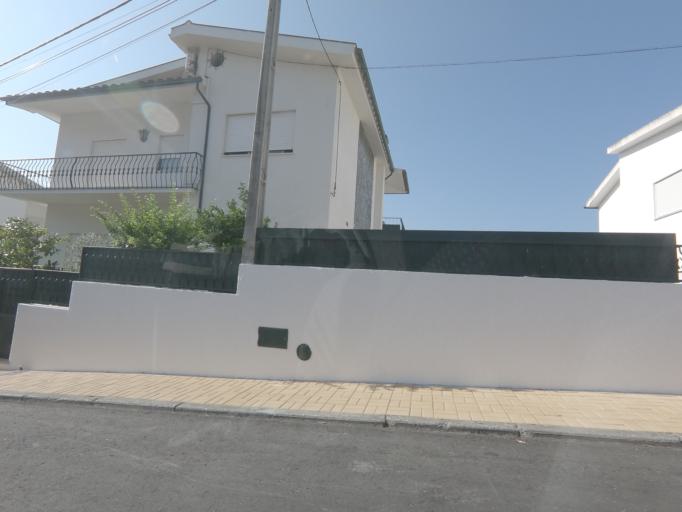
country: PT
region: Vila Real
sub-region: Sabrosa
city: Vilela
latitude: 41.1922
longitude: -7.5457
